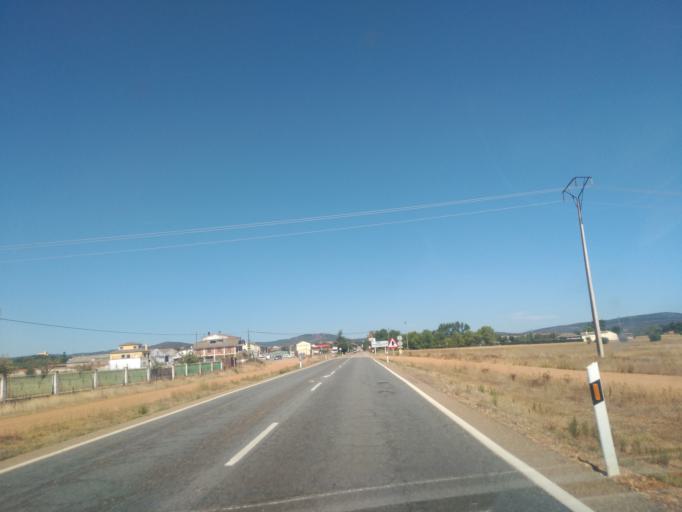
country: ES
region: Castille and Leon
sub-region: Provincia de Zamora
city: Tabara
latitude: 41.8191
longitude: -5.9471
